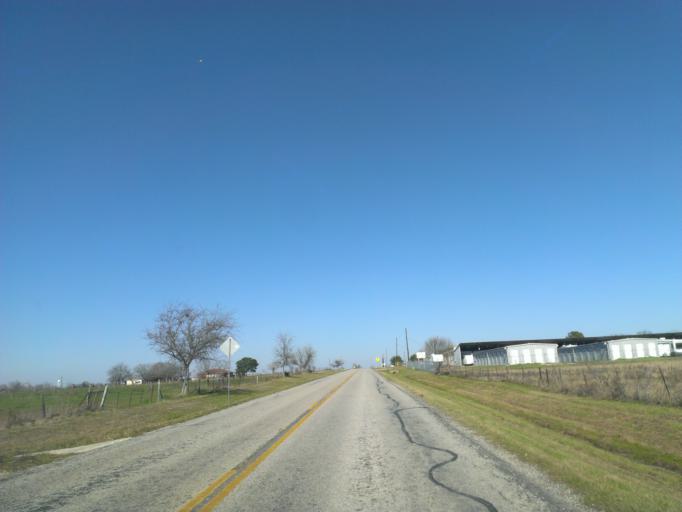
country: US
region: Texas
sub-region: Williamson County
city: Georgetown
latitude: 30.6794
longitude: -97.5882
